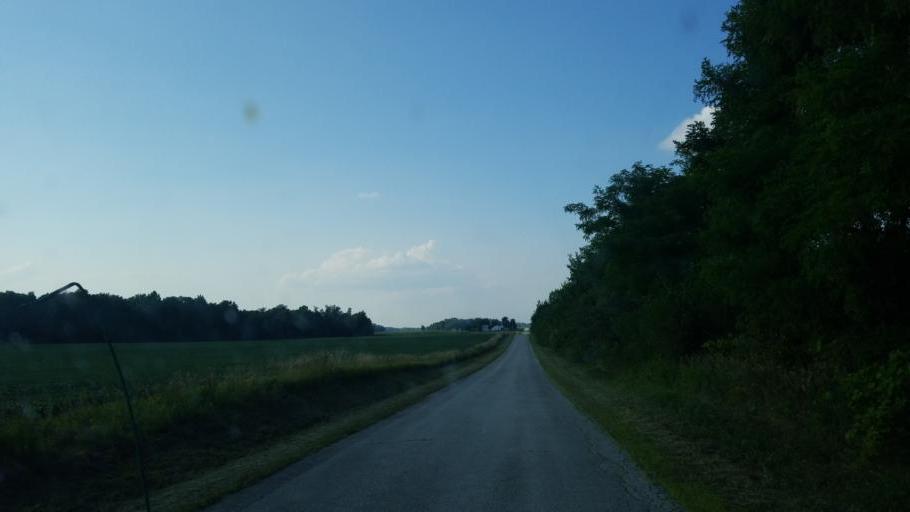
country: US
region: Ohio
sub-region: Crawford County
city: Bucyrus
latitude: 40.8572
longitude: -83.0739
